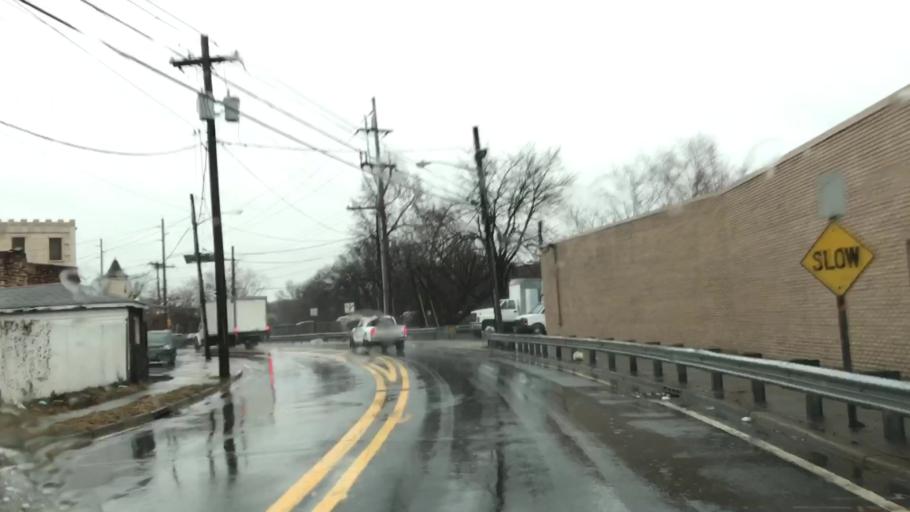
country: US
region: New Jersey
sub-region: Bergen County
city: Wallington
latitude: 40.8657
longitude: -74.1106
